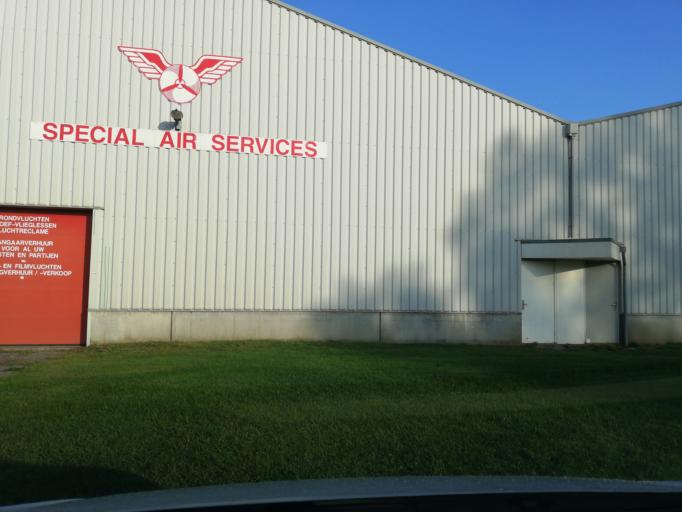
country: NL
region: Gelderland
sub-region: Gemeente Voorst
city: Twello
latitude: 52.2406
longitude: 6.0451
